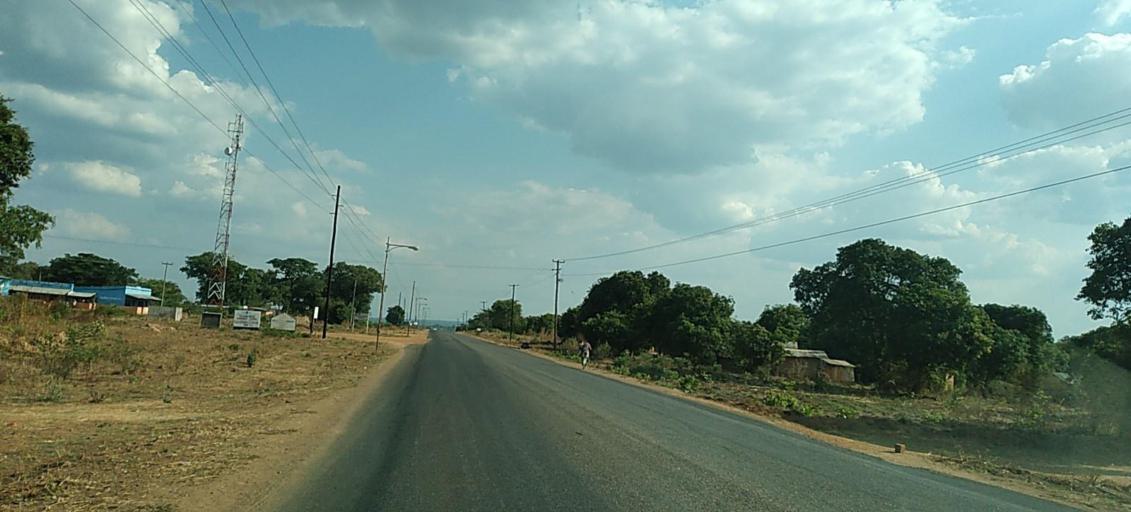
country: ZM
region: Copperbelt
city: Luanshya
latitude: -13.3225
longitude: 28.4151
